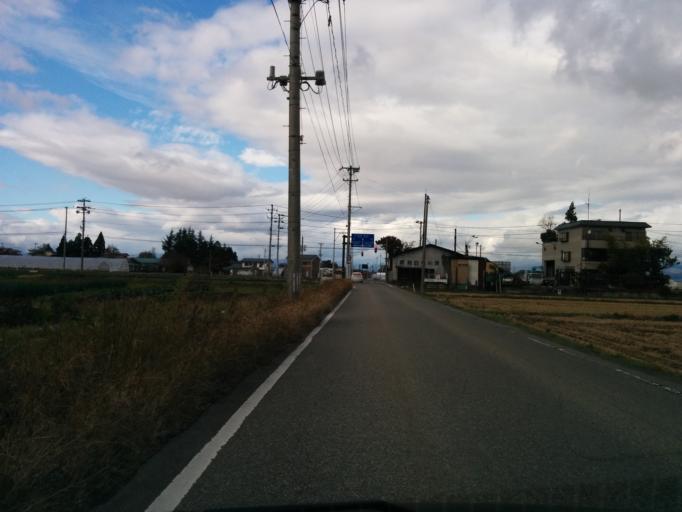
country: JP
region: Fukushima
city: Kitakata
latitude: 37.5031
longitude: 139.9063
